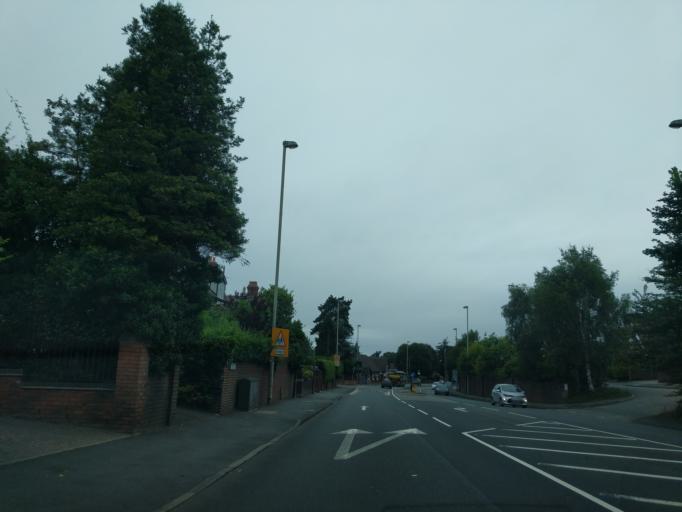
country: GB
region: England
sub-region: Worcestershire
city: Hagley
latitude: 52.4362
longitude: -2.1326
